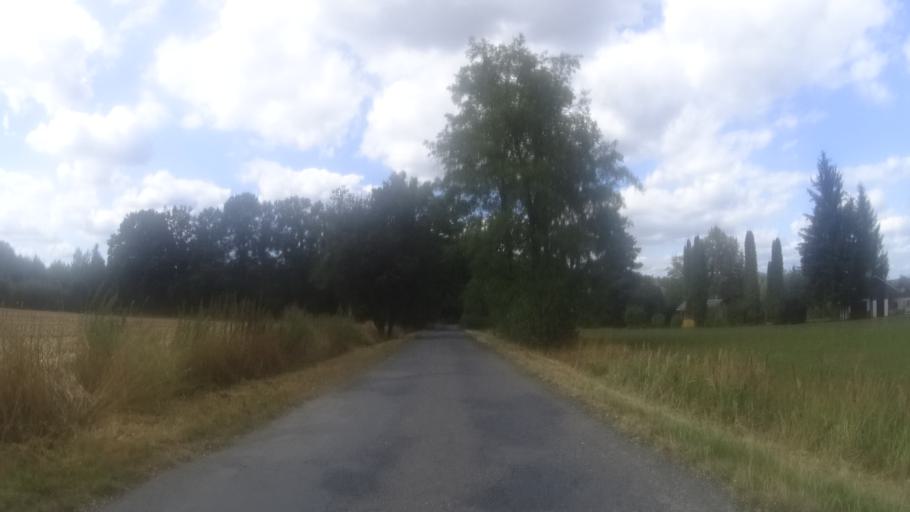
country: CZ
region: Pardubicky
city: Horni Jeleni
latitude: 50.0466
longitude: 16.1575
